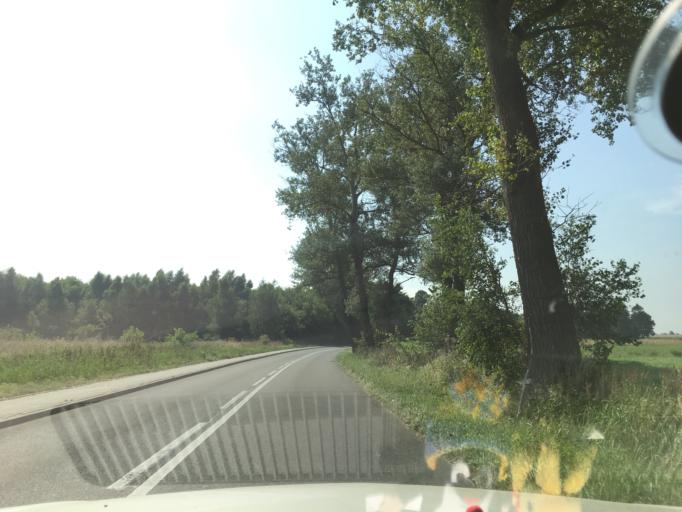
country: PL
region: West Pomeranian Voivodeship
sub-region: Powiat gryficki
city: Pobierowo
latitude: 54.0325
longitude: 14.8740
